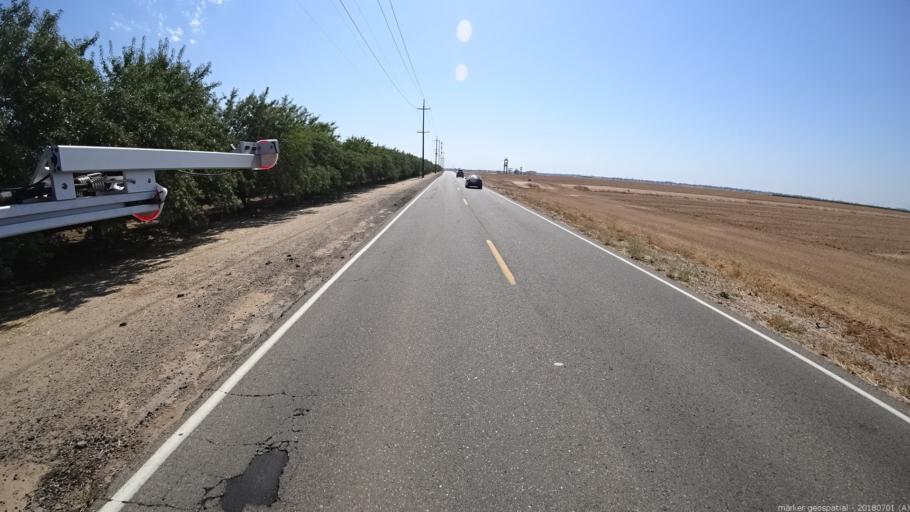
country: US
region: California
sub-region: Madera County
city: Bonadelle Ranchos-Madera Ranchos
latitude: 36.8802
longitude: -119.8281
